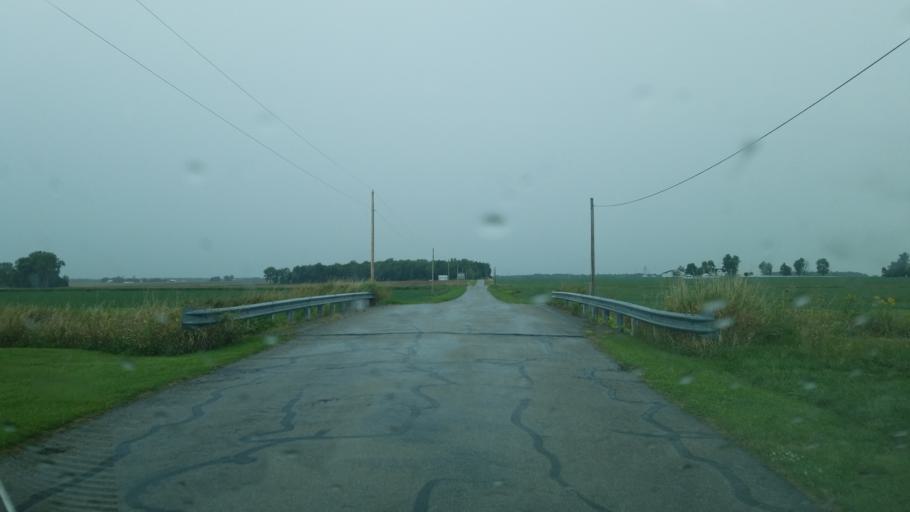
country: US
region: Ohio
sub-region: Huron County
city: Willard
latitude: 41.0265
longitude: -82.8126
